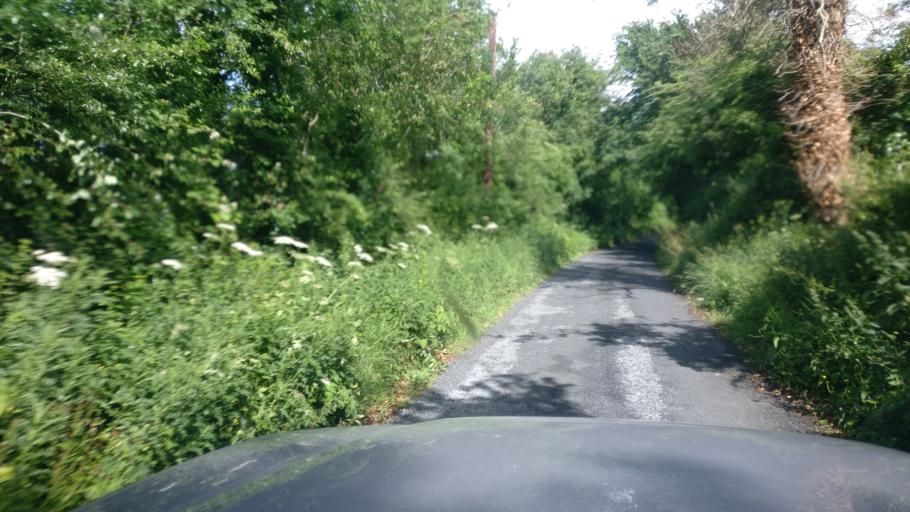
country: IE
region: Connaught
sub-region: County Galway
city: Gort
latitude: 53.0795
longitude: -8.7561
